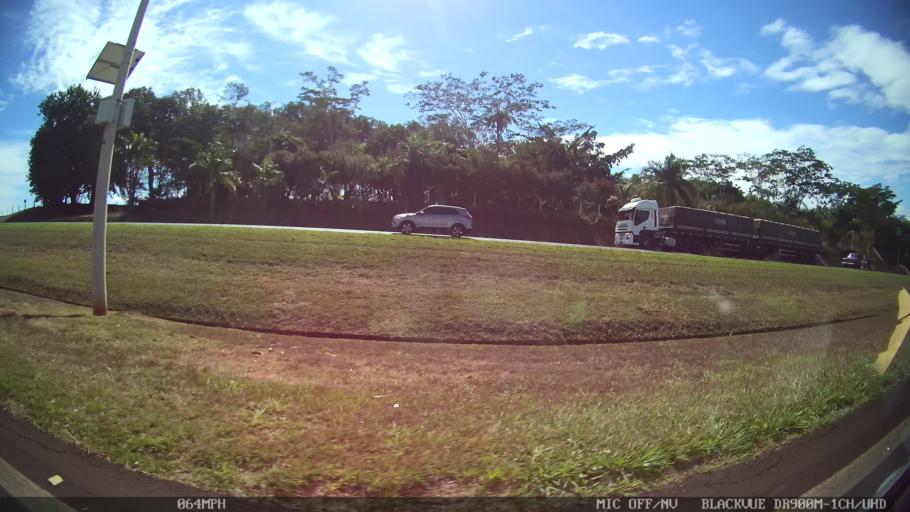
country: BR
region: Sao Paulo
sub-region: Sao Jose Do Rio Preto
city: Sao Jose do Rio Preto
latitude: -20.8157
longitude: -49.4545
